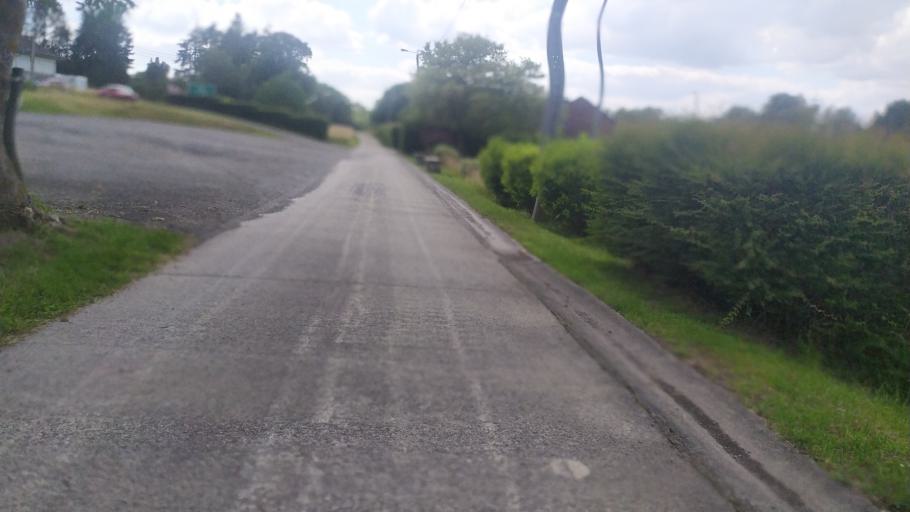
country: BE
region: Wallonia
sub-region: Province du Luxembourg
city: Wellin
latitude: 50.0801
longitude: 5.1045
